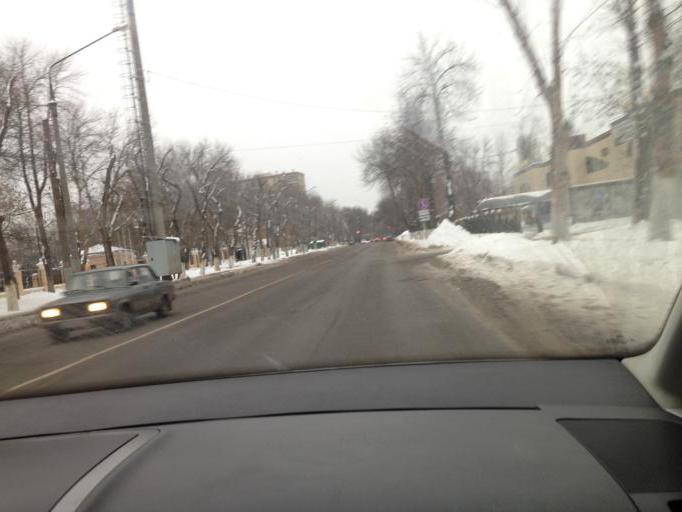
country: RU
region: Voronezj
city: Voronezh
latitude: 51.6412
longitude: 39.1771
